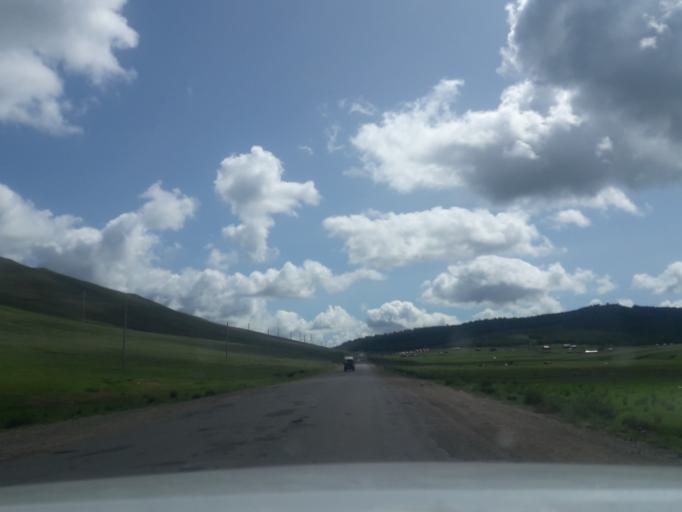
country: MN
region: Central Aimak
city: Ihsueuej
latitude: 48.1564
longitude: 106.4061
